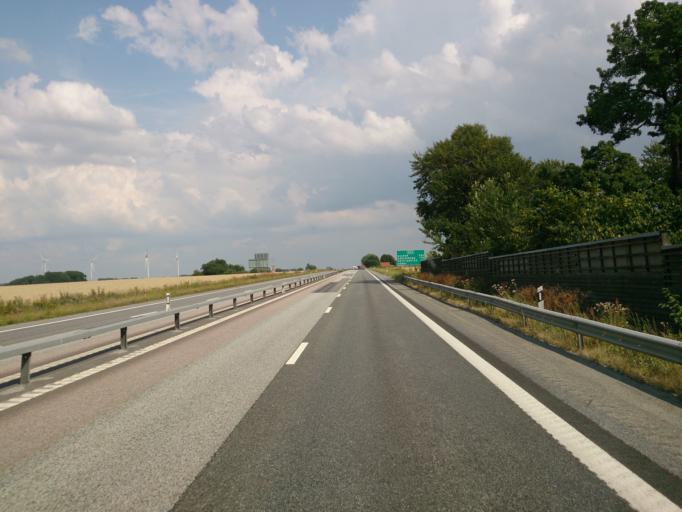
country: SE
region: Skane
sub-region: Eslovs Kommun
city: Eslov
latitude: 55.7776
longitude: 13.3728
